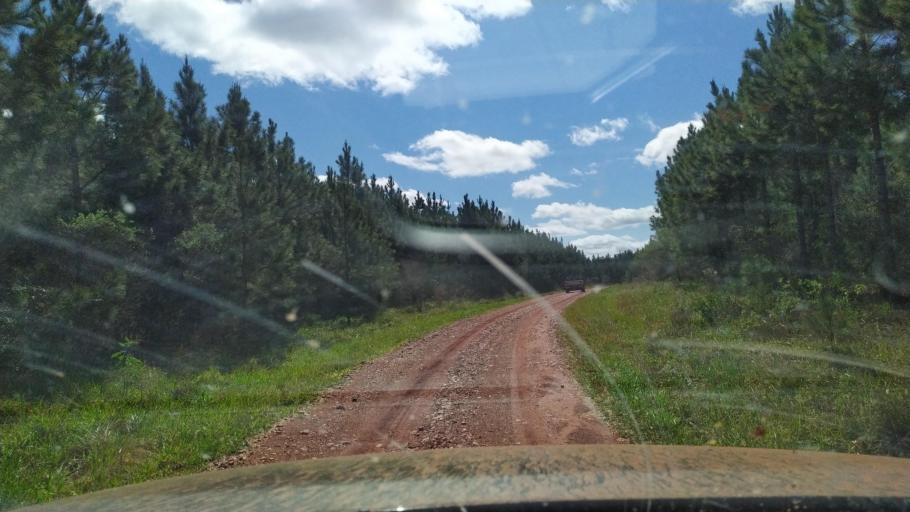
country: AR
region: Corrientes
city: Santo Tome
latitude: -28.4654
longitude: -55.9820
